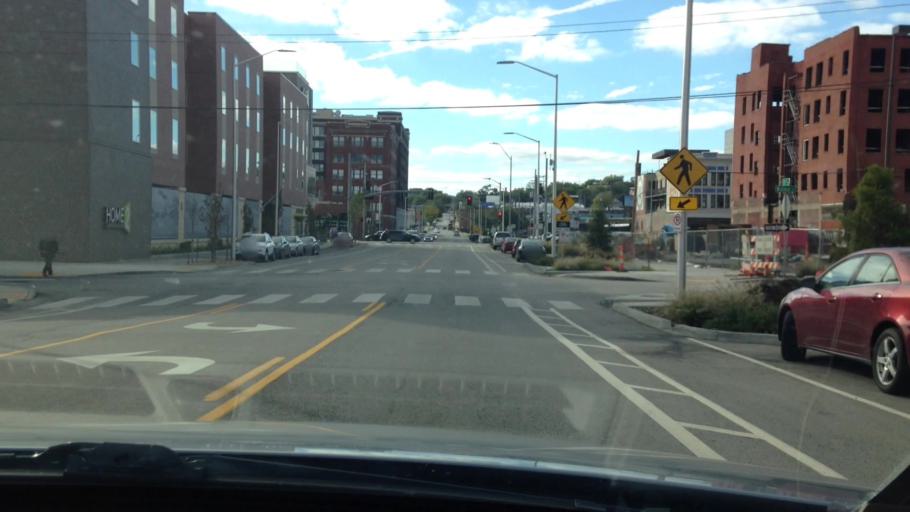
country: US
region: Missouri
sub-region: Jackson County
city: Kansas City
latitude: 39.0891
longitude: -94.5823
